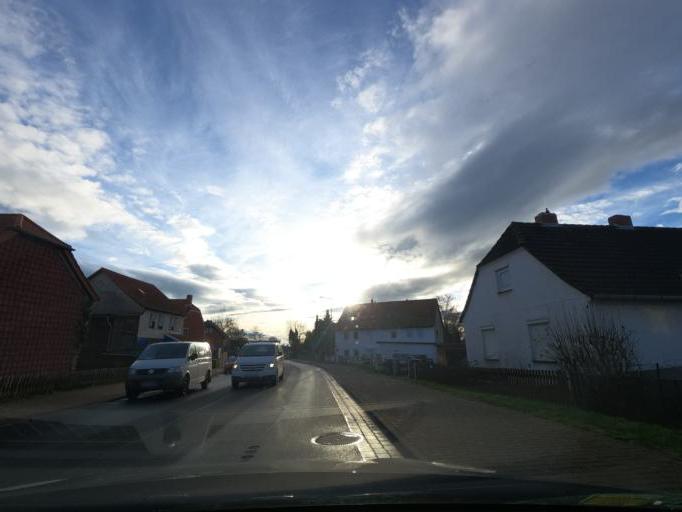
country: DE
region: Lower Saxony
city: Ohrum
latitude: 52.1536
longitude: 10.5881
